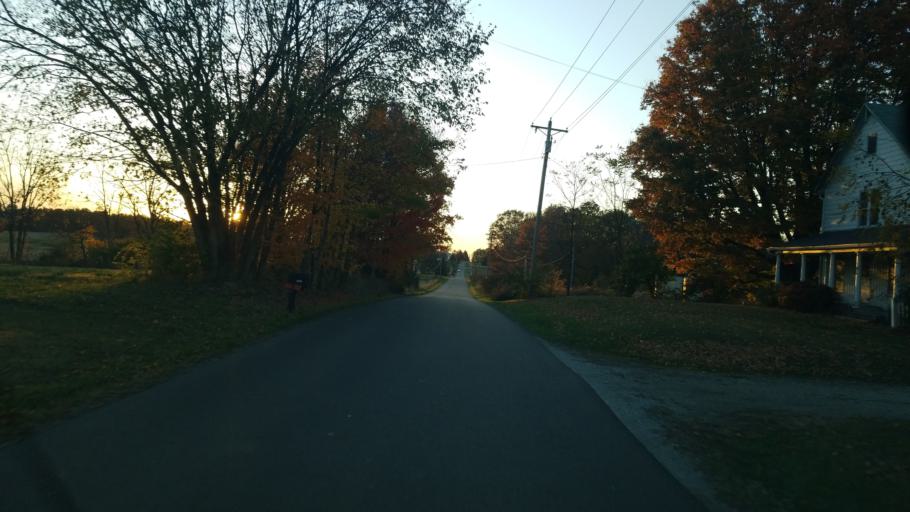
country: US
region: Ohio
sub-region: Morrow County
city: Mount Gilead
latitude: 40.5151
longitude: -82.7965
